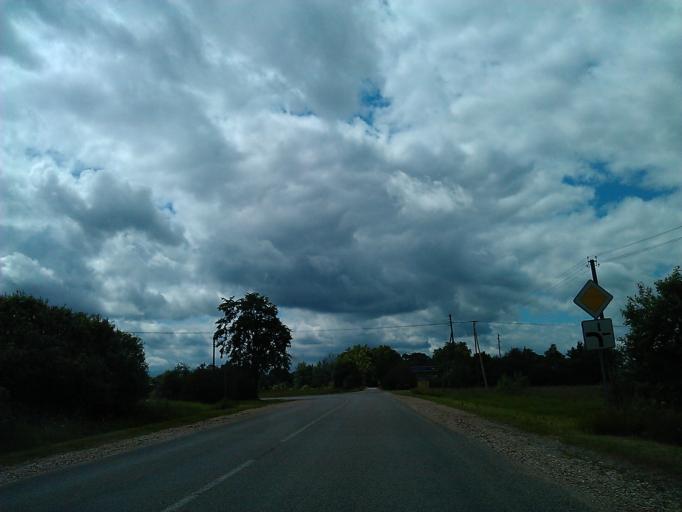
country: LV
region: Talsu Rajons
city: Stende
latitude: 57.0783
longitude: 22.2927
